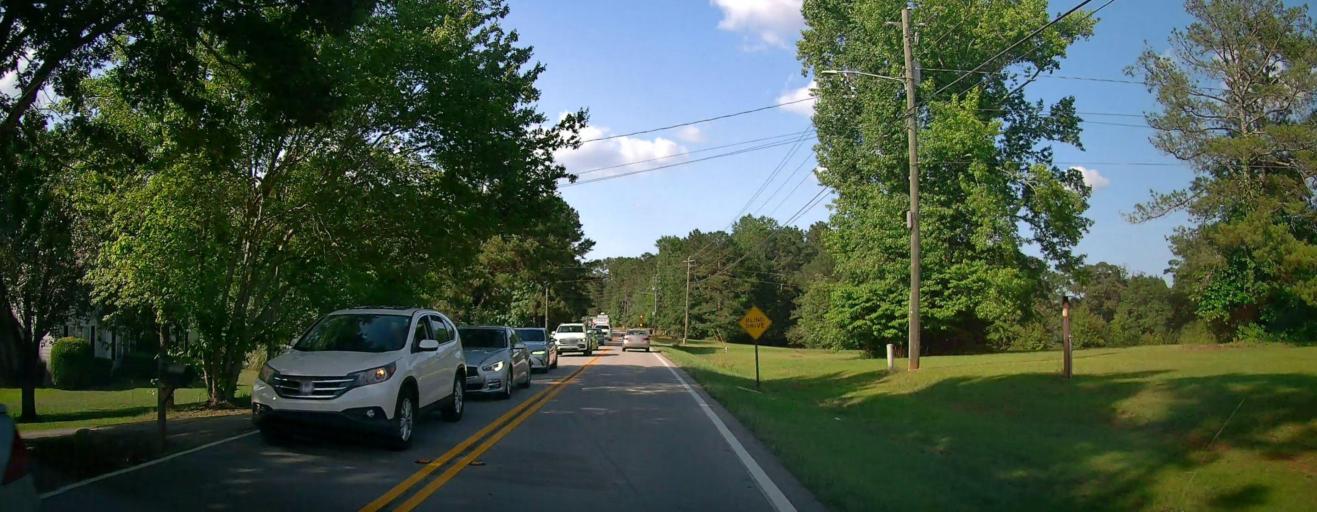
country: US
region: Georgia
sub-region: Henry County
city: Stockbridge
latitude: 33.4708
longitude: -84.2293
